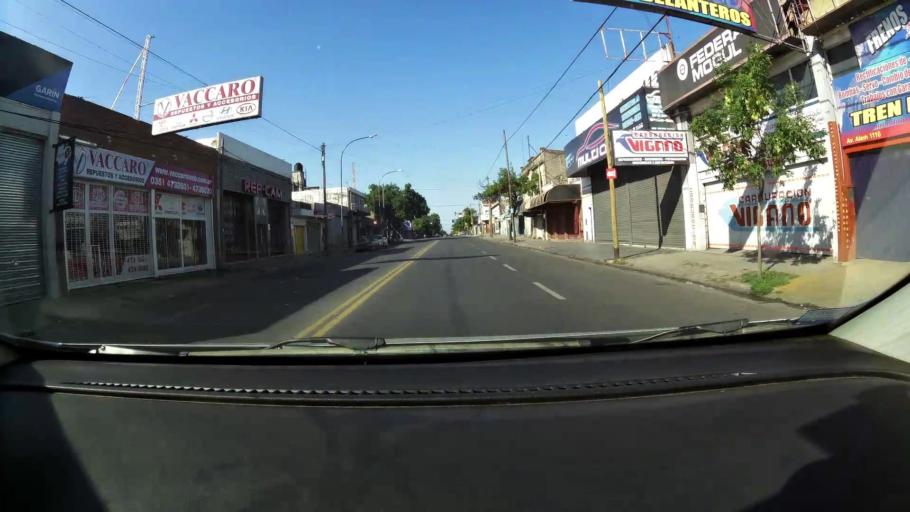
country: AR
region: Cordoba
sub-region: Departamento de Capital
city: Cordoba
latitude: -31.3903
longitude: -64.1635
